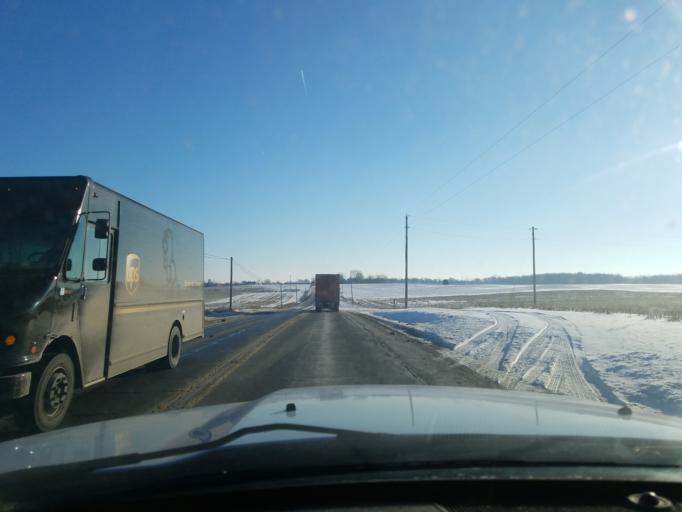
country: US
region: Indiana
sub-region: Noble County
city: Kendallville
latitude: 41.4525
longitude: -85.3220
